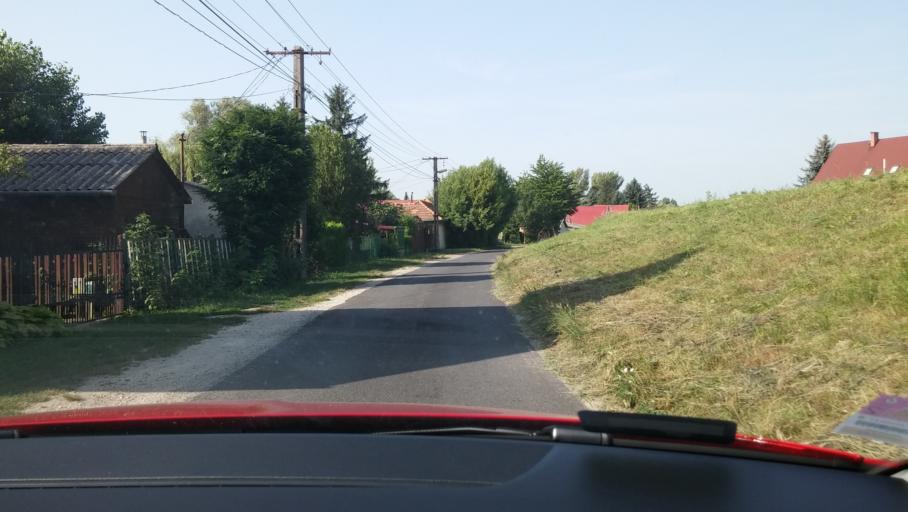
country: HU
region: Pest
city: Rackeve
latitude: 47.1755
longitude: 18.9454
